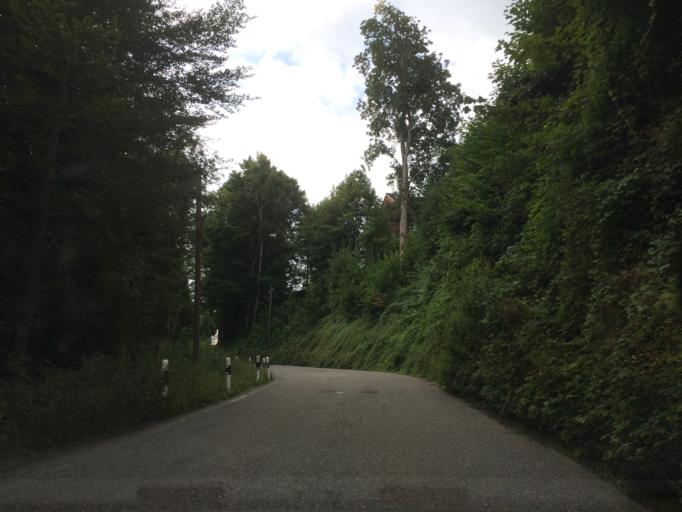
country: CH
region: Appenzell Ausserrhoden
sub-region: Bezirk Mittelland
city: Trogen
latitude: 47.4061
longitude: 9.4640
